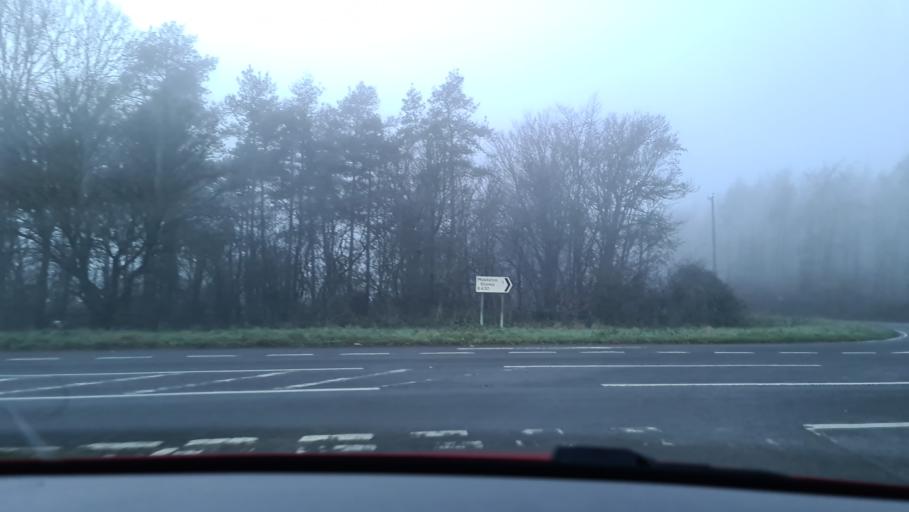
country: GB
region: England
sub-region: Oxfordshire
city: Bicester
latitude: 51.8941
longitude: -1.2256
